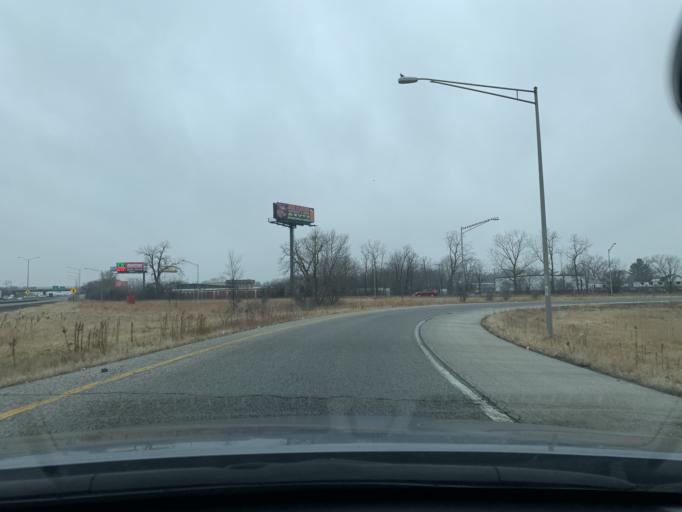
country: US
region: Illinois
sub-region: Cook County
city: Markham
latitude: 41.6011
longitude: -87.7105
